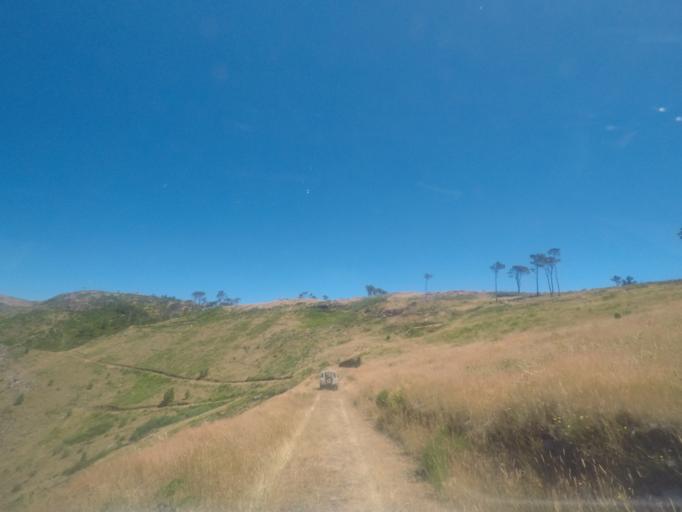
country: PT
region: Madeira
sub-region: Funchal
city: Nossa Senhora do Monte
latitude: 32.7138
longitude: -16.9124
